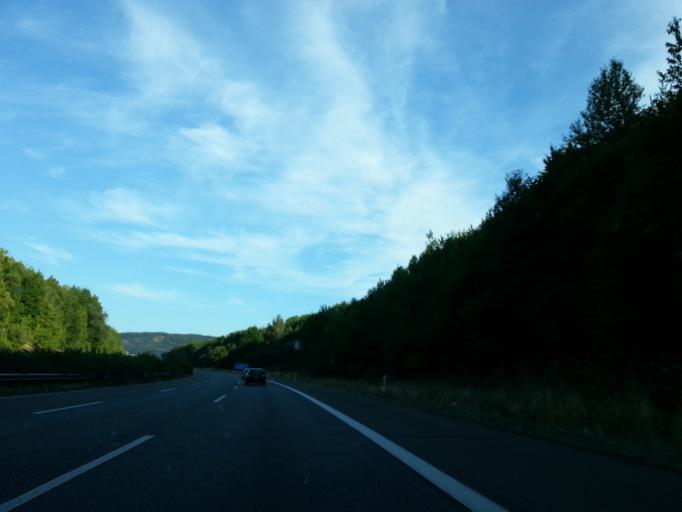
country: DE
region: Rheinland-Pfalz
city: Schweich
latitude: 49.8026
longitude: 6.7615
